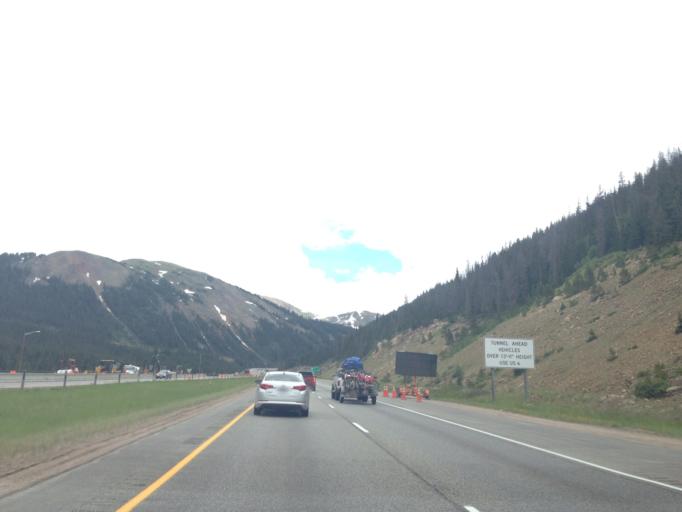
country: US
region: Colorado
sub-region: Summit County
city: Keystone
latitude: 39.6915
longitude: -105.8794
